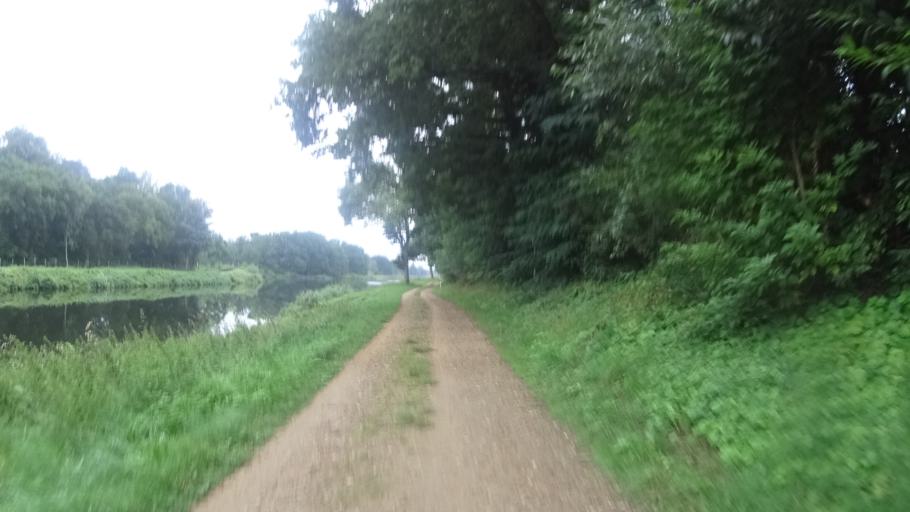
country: DE
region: Schleswig-Holstein
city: Witzeeze
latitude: 53.4629
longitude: 10.6268
